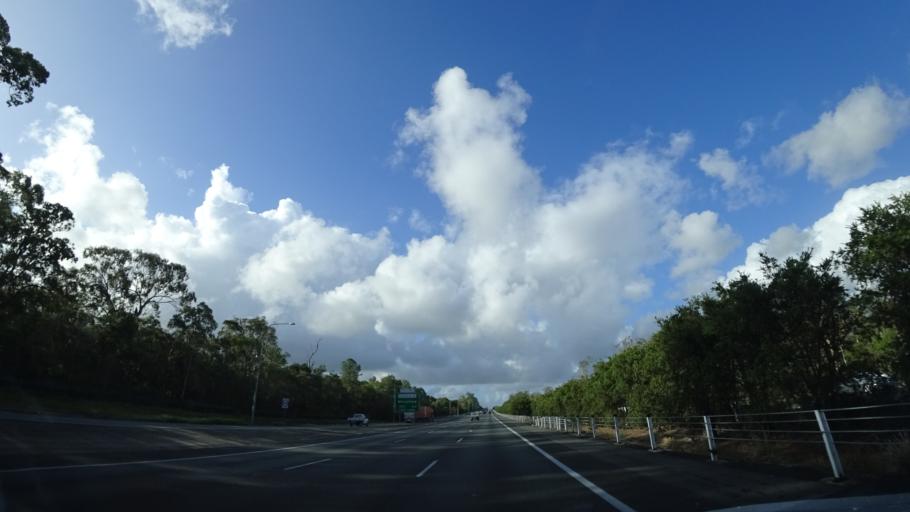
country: AU
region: Queensland
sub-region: Moreton Bay
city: Morayfield
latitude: -27.1214
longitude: 152.9770
